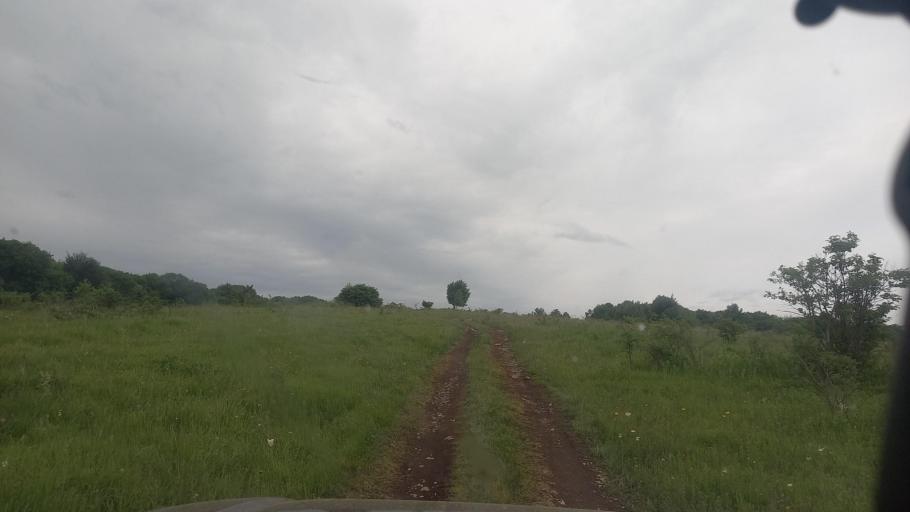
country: RU
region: Karachayevo-Cherkesiya
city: Pregradnaya
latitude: 44.0219
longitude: 41.2925
